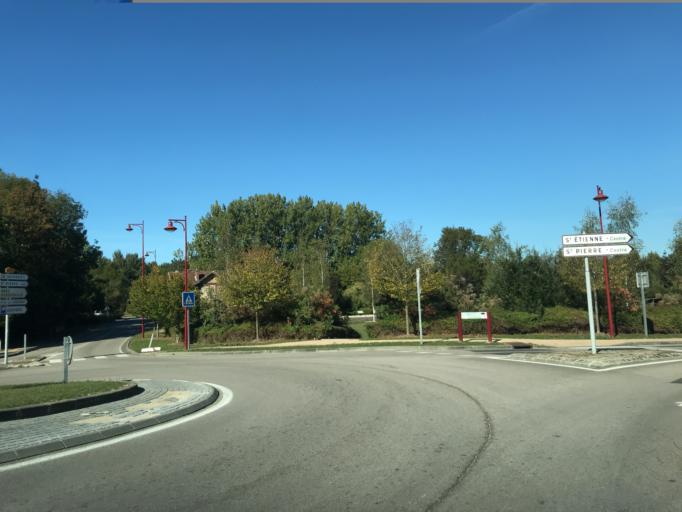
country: FR
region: Haute-Normandie
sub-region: Departement de l'Eure
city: Le Vaudreuil
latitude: 49.2469
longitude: 1.2100
